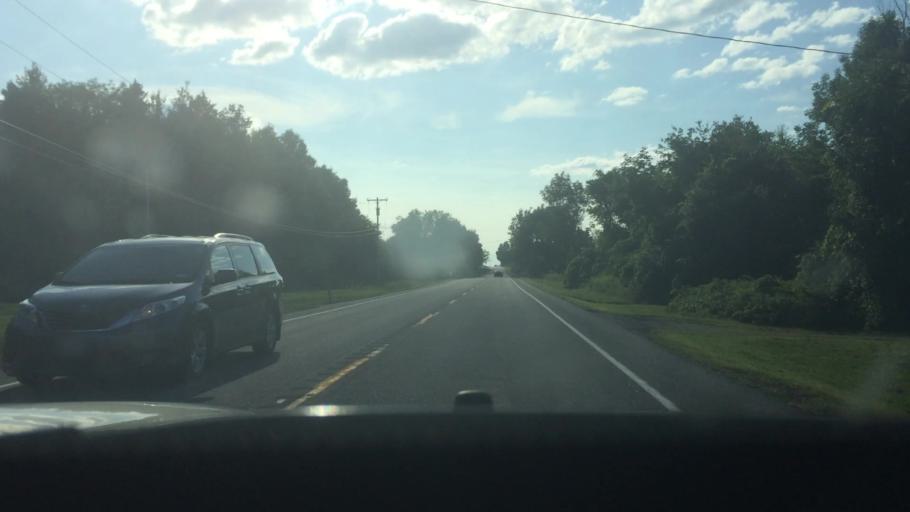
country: US
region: New York
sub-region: St. Lawrence County
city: Potsdam
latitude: 44.6895
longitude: -74.7351
